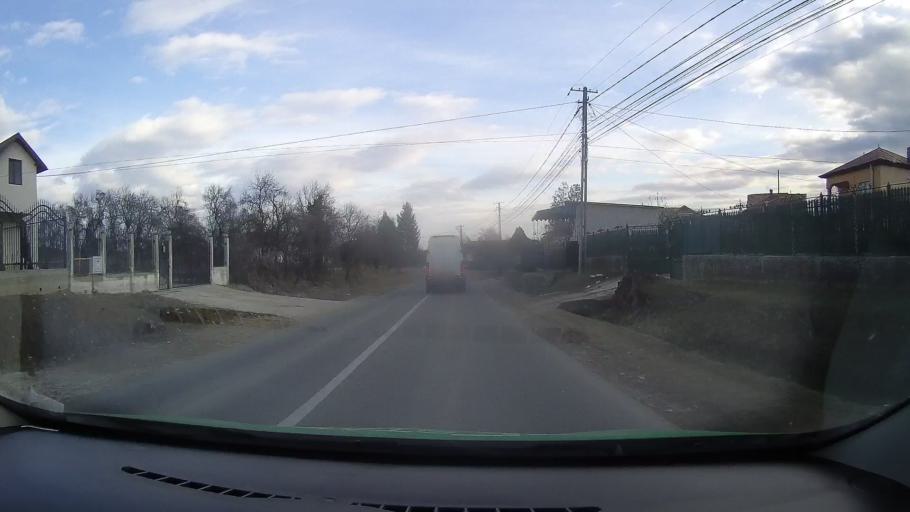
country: RO
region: Dambovita
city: Razvad
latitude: 44.9345
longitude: 25.5396
